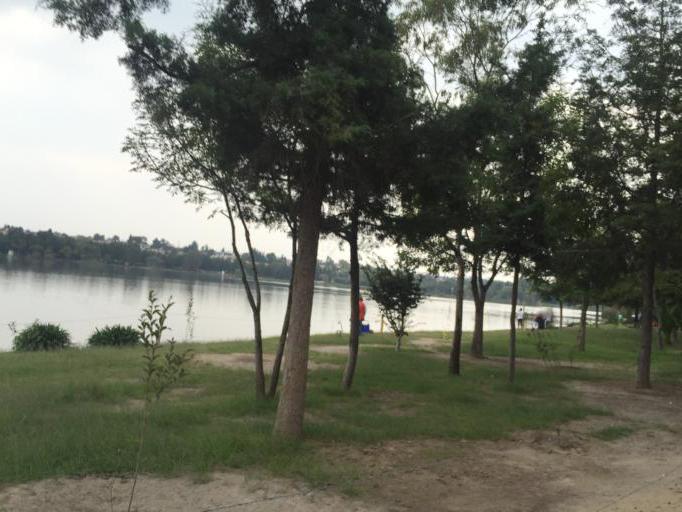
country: MX
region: Mexico
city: Cuautitlan Izcalli
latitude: 19.6548
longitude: -99.2219
